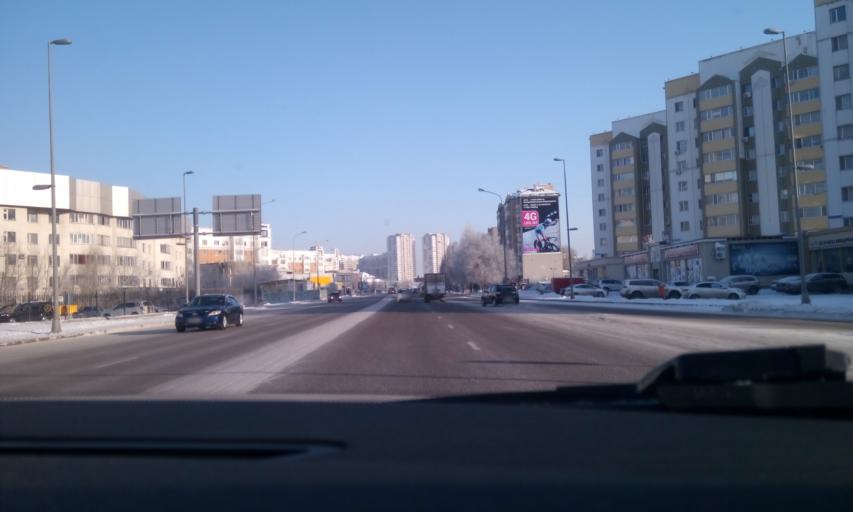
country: KZ
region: Astana Qalasy
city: Astana
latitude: 51.1560
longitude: 71.4341
